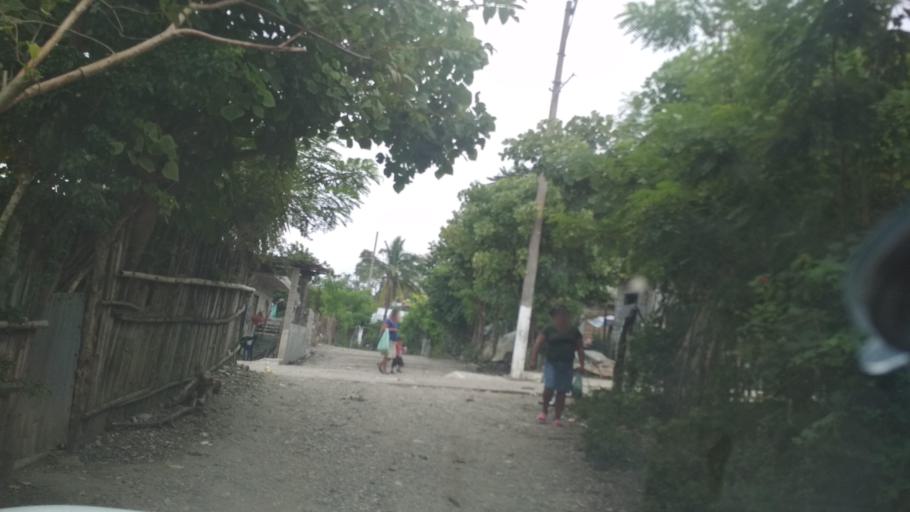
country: MX
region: Veracruz
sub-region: Poza Rica de Hidalgo
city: El Mollejon
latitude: 20.5333
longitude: -97.3884
